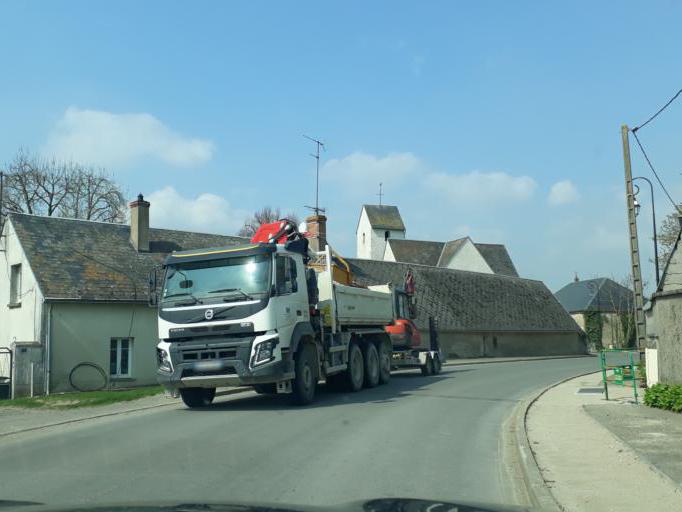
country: FR
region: Centre
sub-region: Departement d'Eure-et-Loir
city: Baigneaux
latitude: 48.0990
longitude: 1.8409
